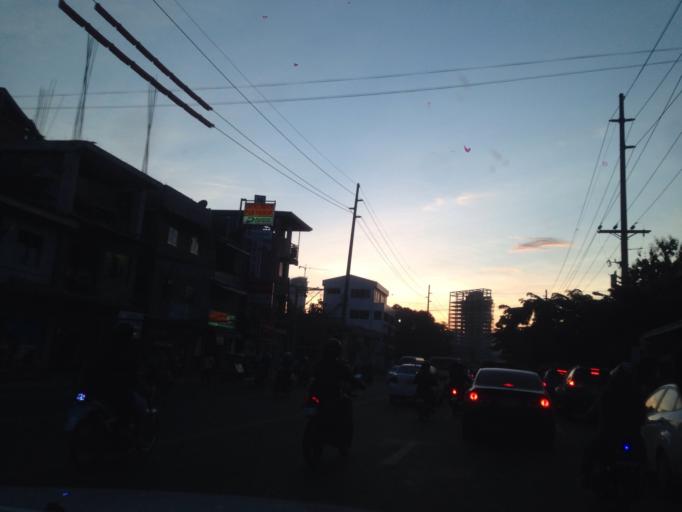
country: PH
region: Central Visayas
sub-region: Cebu City
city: Baugo
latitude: 10.3080
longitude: 123.9085
